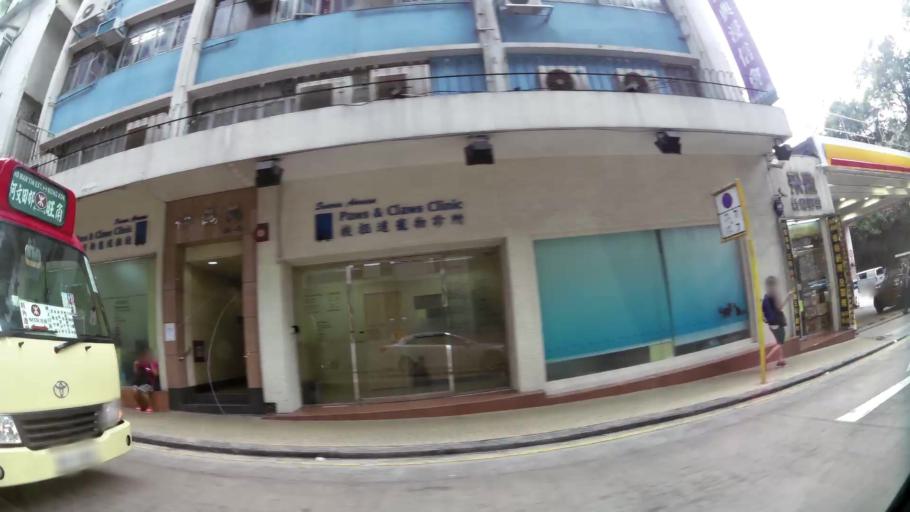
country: HK
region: Kowloon City
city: Kowloon
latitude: 22.3199
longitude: 114.1747
